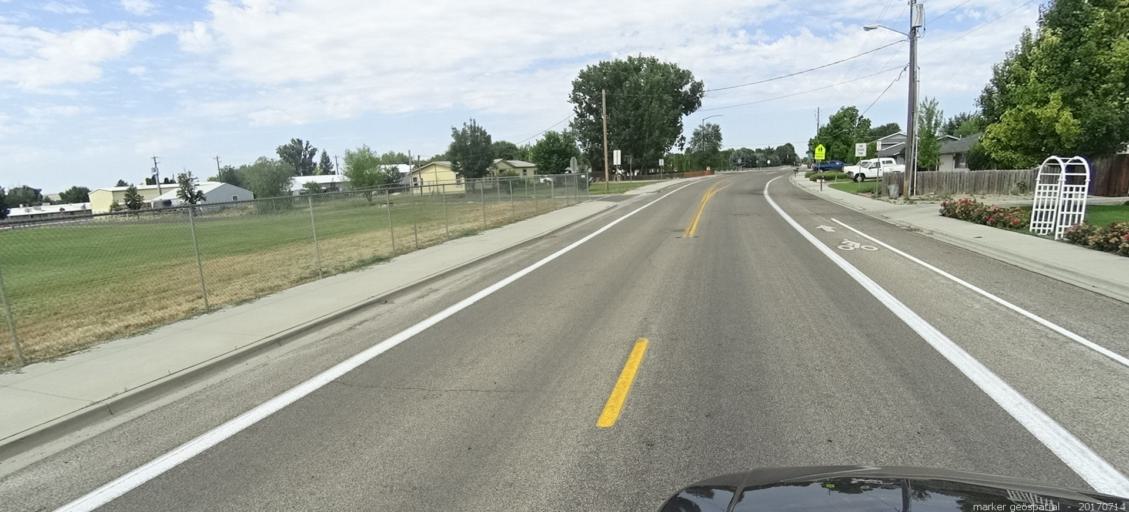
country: US
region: Idaho
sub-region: Ada County
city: Kuna
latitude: 43.4958
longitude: -116.4220
